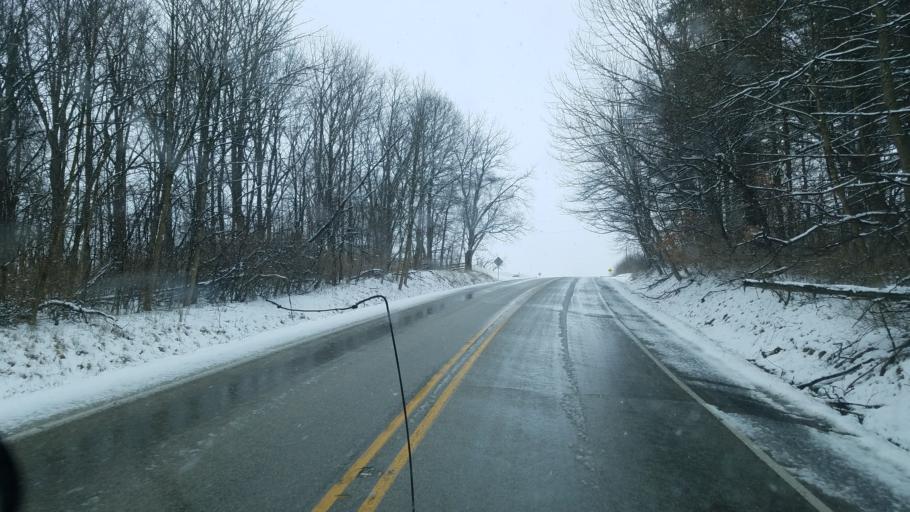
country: US
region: Indiana
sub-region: Randolph County
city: Lynn
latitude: 39.9496
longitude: -84.9910
